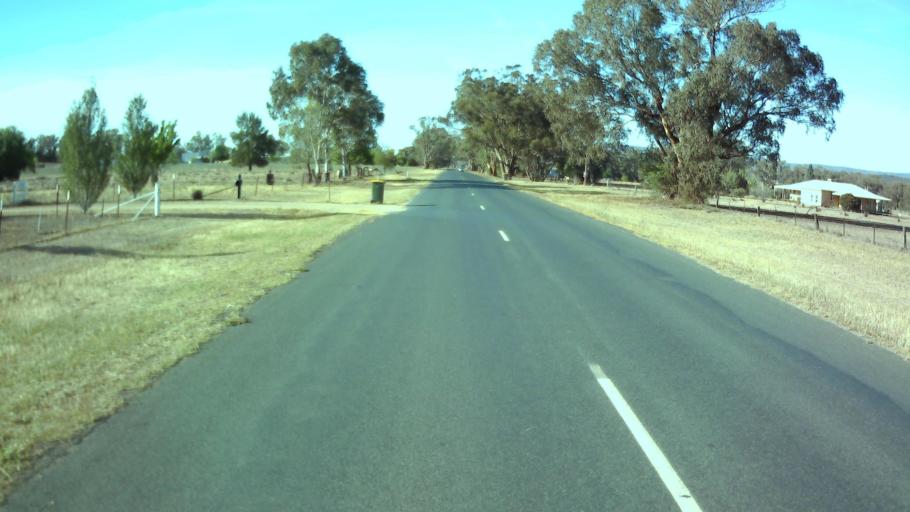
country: AU
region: New South Wales
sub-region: Weddin
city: Grenfell
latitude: -33.9112
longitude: 148.1445
